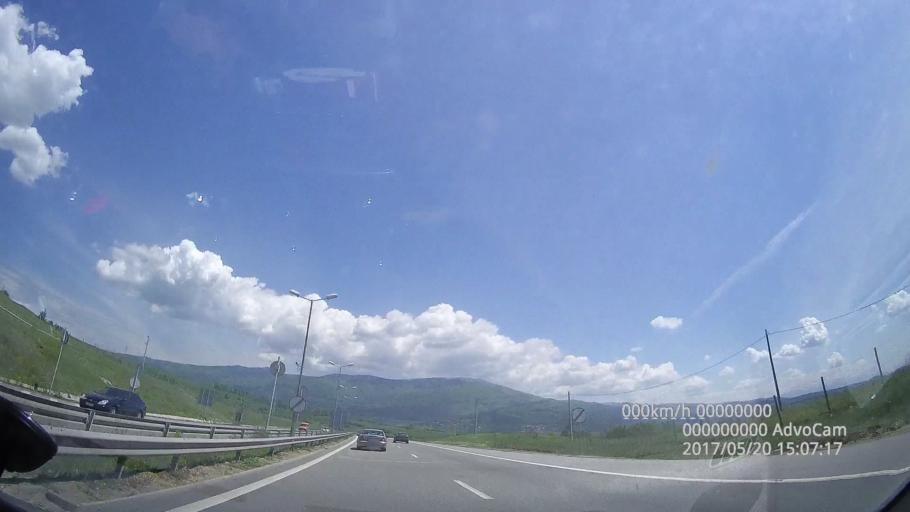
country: BG
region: Pernik
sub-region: Obshtina Pernik
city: Pernik
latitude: 42.6256
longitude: 23.1290
